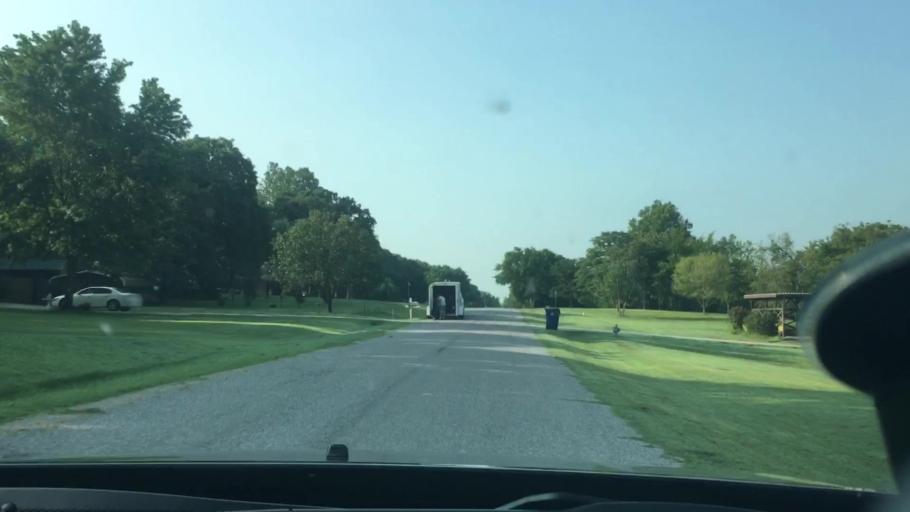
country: US
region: Oklahoma
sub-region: Pontotoc County
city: Ada
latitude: 34.7891
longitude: -96.7397
